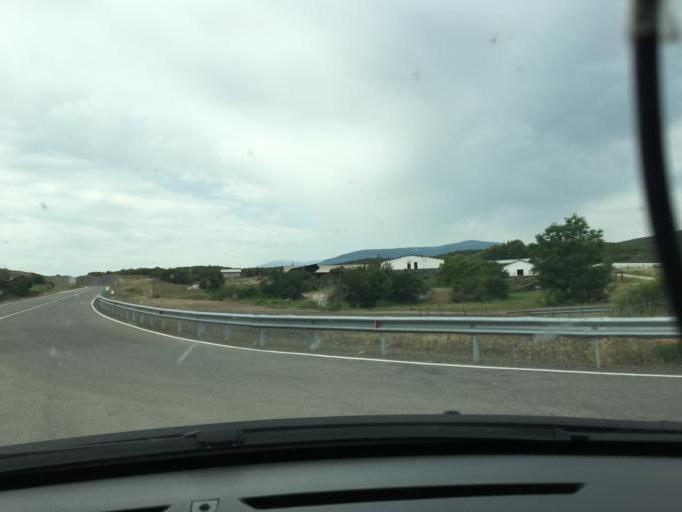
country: MK
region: Gevgelija
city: Miravci
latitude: 41.3039
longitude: 22.4436
